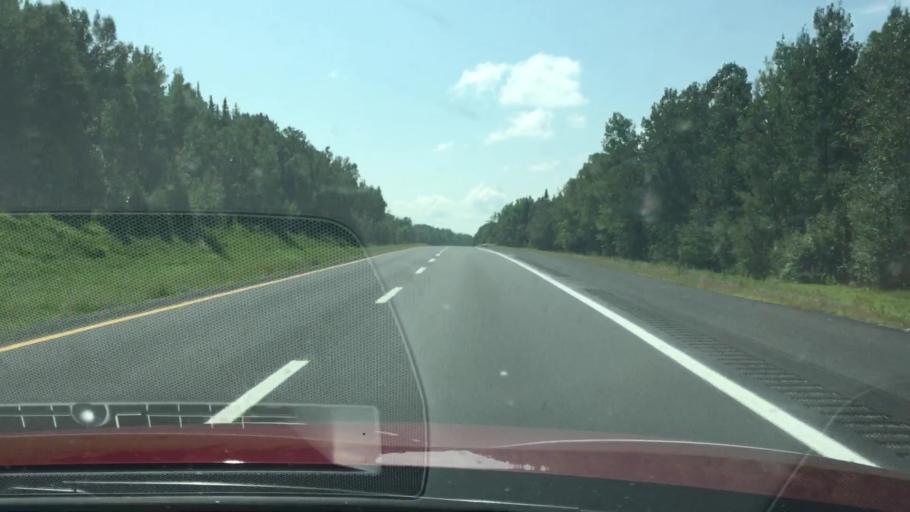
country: US
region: Maine
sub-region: Penobscot County
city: Patten
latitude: 45.9124
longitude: -68.3781
